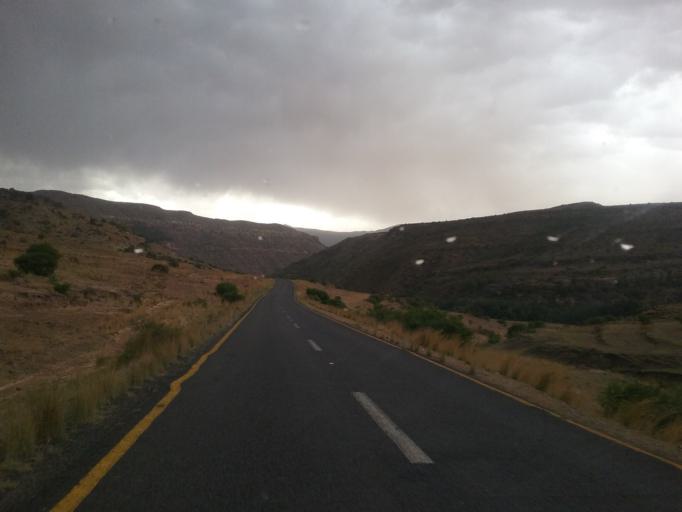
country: LS
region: Quthing
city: Quthing
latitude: -30.2872
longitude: 27.7843
